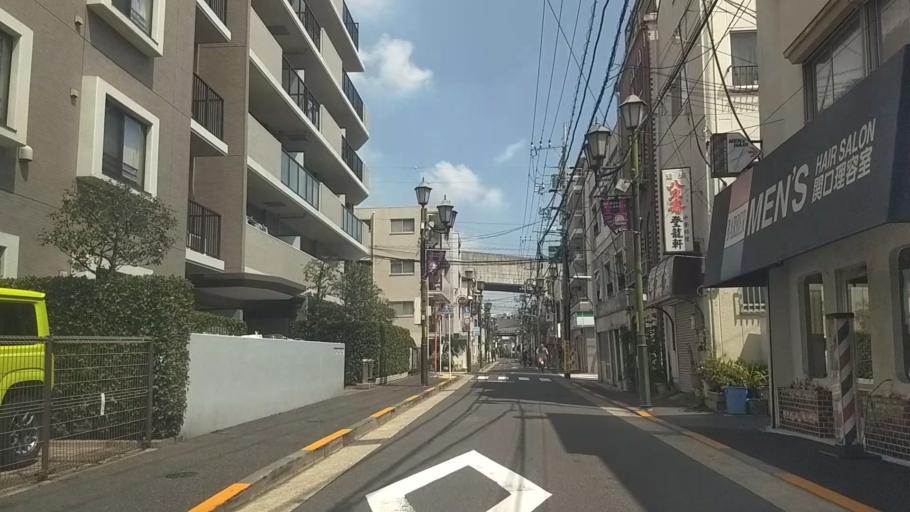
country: JP
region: Kanagawa
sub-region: Kawasaki-shi
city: Kawasaki
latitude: 35.5943
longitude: 139.7182
